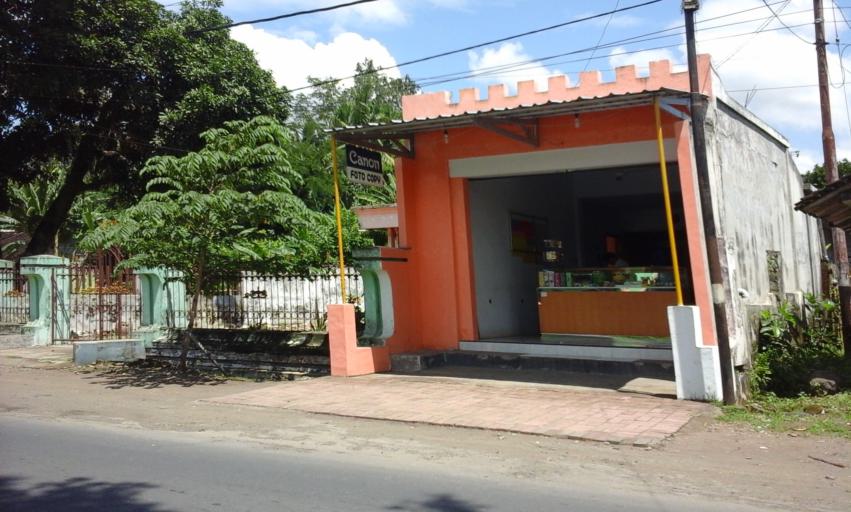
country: ID
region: East Java
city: Sumberketangi
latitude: -8.1861
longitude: 113.7396
